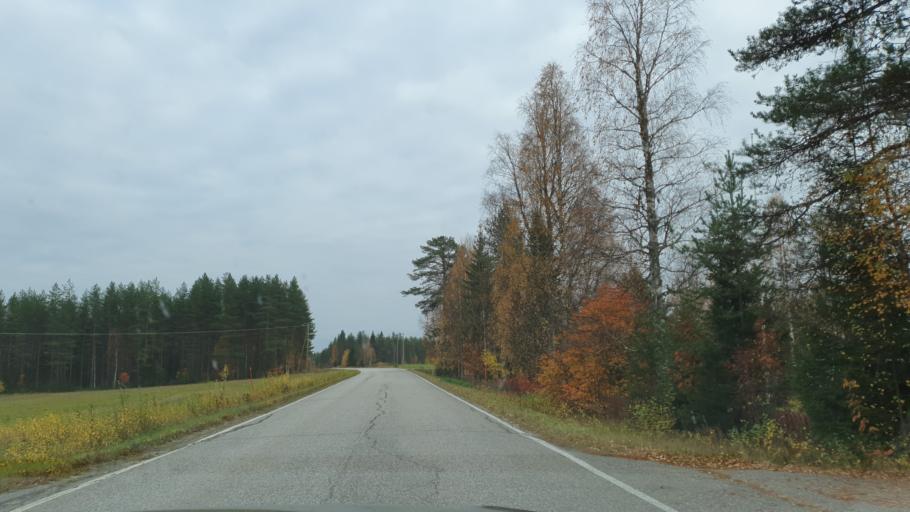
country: FI
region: Kainuu
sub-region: Kajaani
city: Ristijaervi
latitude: 64.4577
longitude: 28.3251
